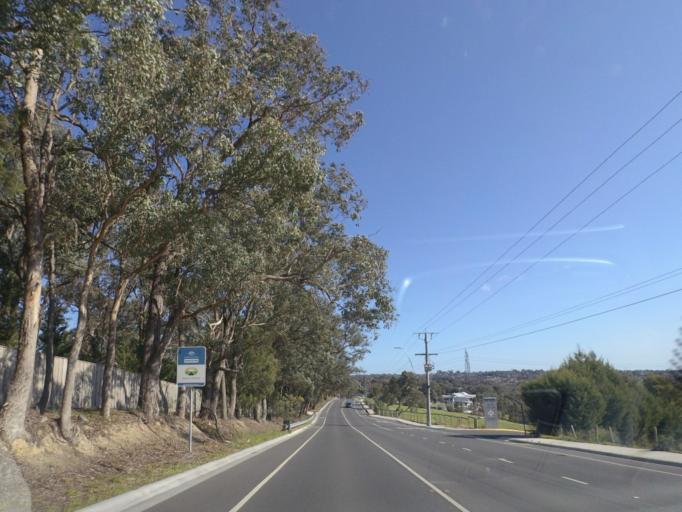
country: AU
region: Victoria
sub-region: Manningham
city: Park Orchards
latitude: -37.7721
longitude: 145.1984
